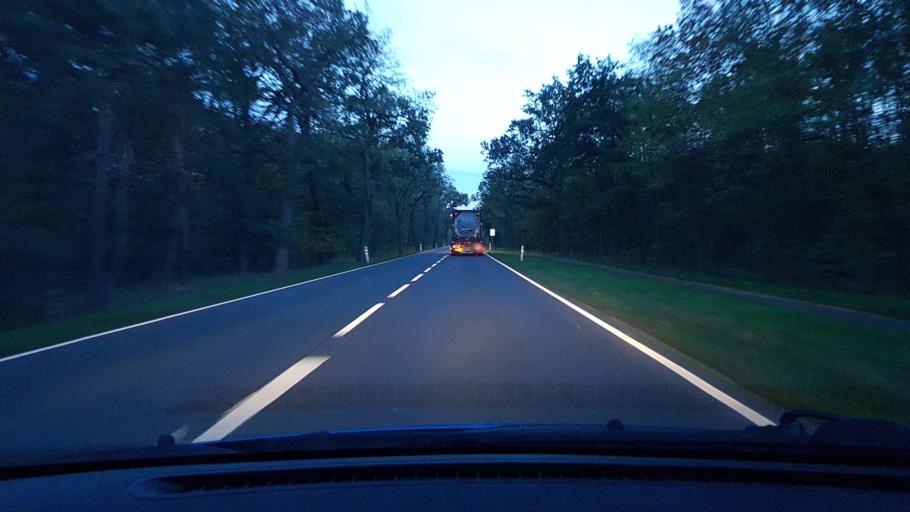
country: DE
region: Saxony-Anhalt
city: Zerbst
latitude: 51.9476
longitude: 12.1114
